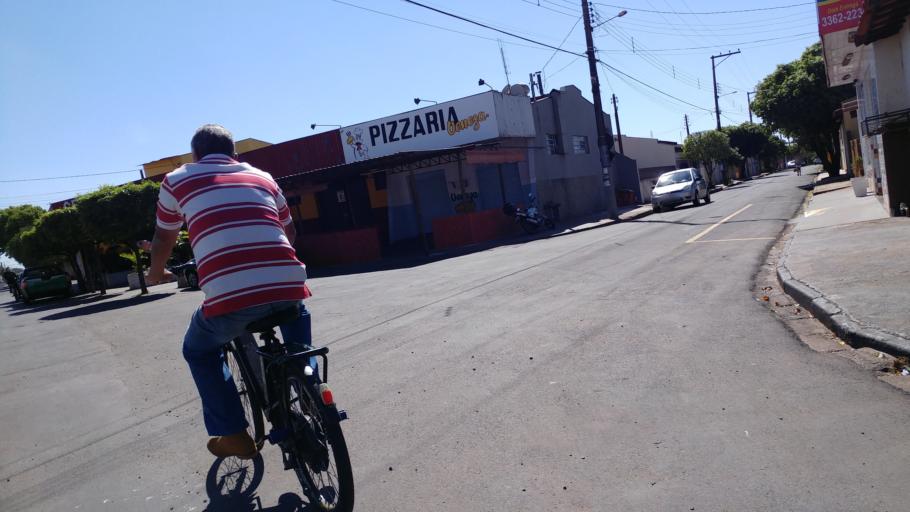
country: BR
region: Sao Paulo
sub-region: Paraguacu Paulista
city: Paraguacu Paulista
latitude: -22.4296
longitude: -50.5832
